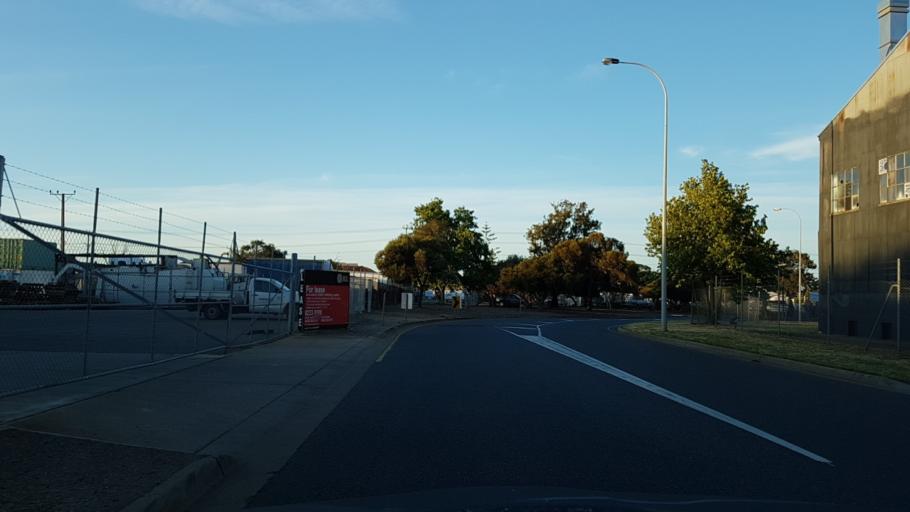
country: AU
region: South Australia
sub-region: Charles Sturt
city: Woodville North
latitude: -34.8607
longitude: 138.5377
